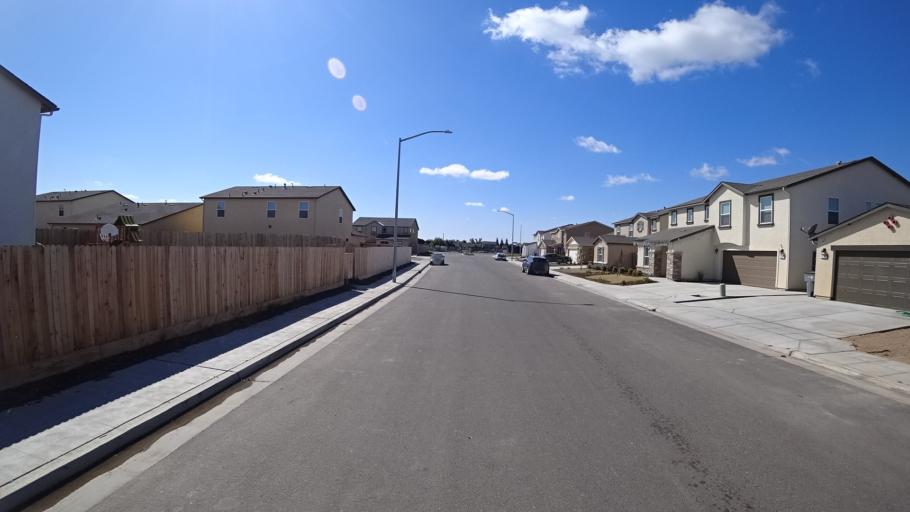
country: US
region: California
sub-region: Fresno County
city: West Park
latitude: 36.7873
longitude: -119.8912
